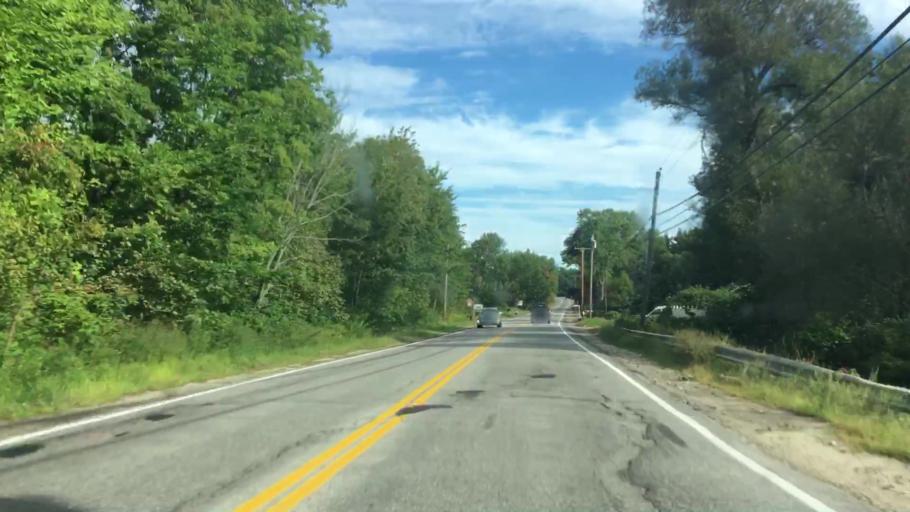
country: US
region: Maine
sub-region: Cumberland County
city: Falmouth
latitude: 43.7495
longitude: -70.2989
